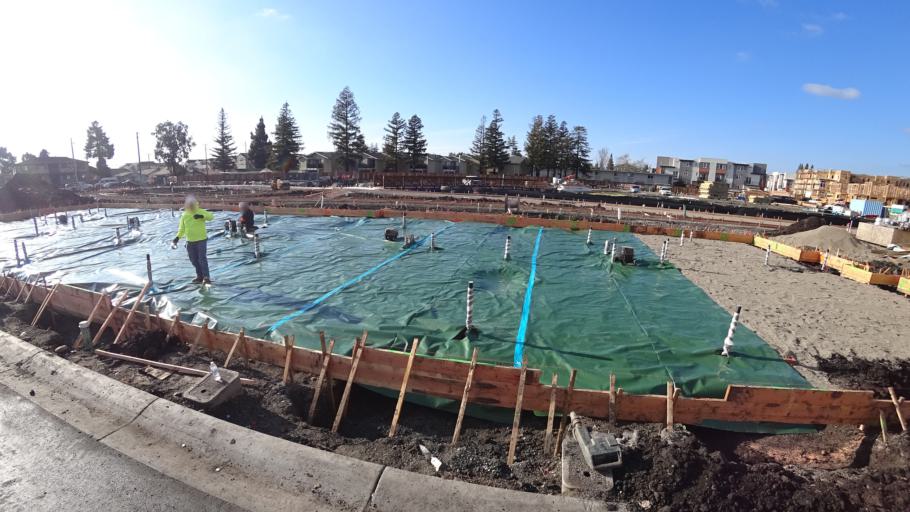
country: US
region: California
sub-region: Alameda County
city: Union City
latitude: 37.6308
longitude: -122.0506
